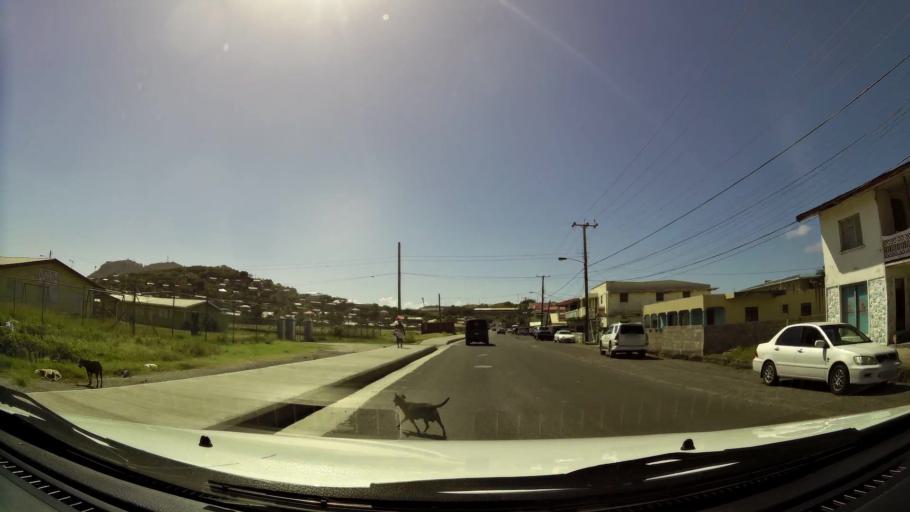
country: LC
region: Vieux-Fort
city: Vieux Fort
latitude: 13.7286
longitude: -60.9517
